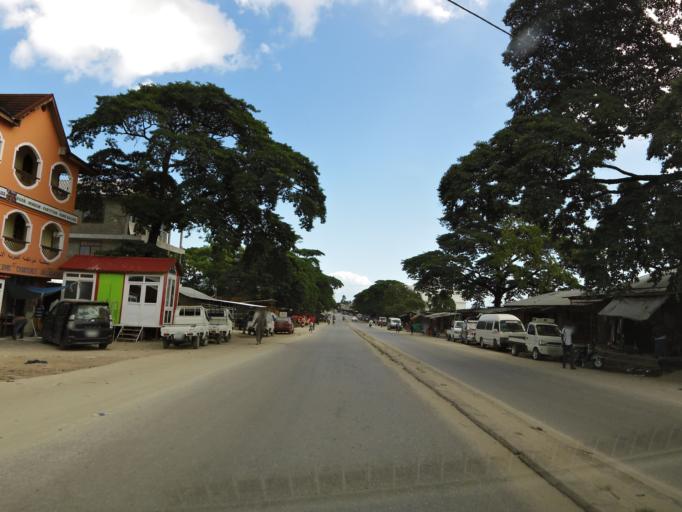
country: TZ
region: Zanzibar Urban/West
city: Zanzibar
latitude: -6.1638
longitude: 39.2196
